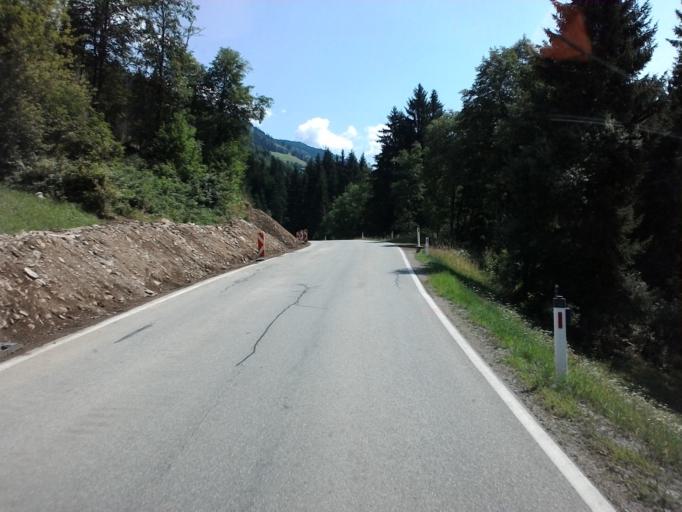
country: AT
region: Tyrol
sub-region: Politischer Bezirk Lienz
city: Untertilliach
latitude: 46.7043
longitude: 12.6935
